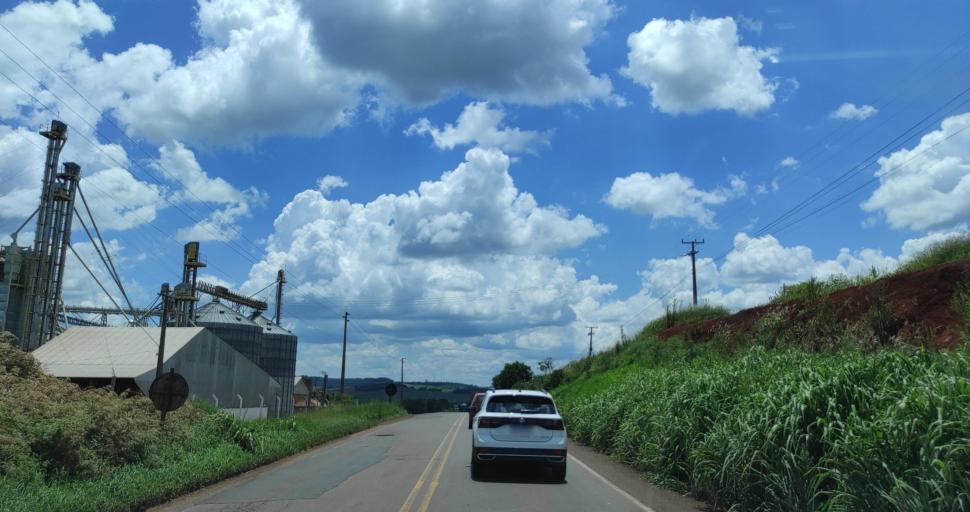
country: BR
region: Santa Catarina
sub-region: Xanxere
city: Xanxere
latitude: -26.7637
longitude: -52.4044
